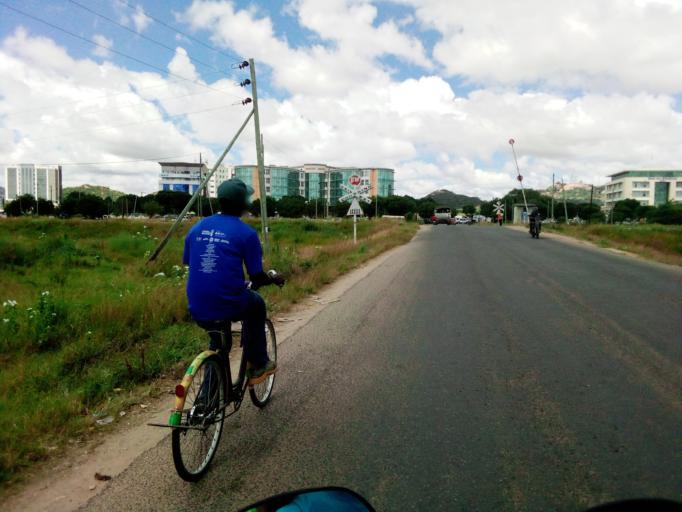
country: TZ
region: Dodoma
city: Dodoma
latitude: -6.1849
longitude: 35.7586
